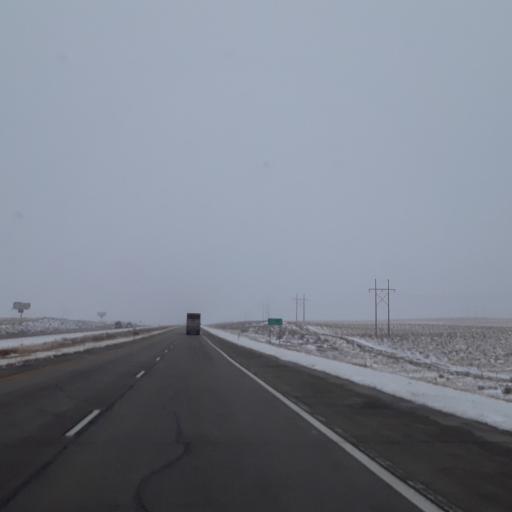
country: US
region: Colorado
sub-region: Logan County
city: Sterling
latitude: 40.7151
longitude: -103.0439
